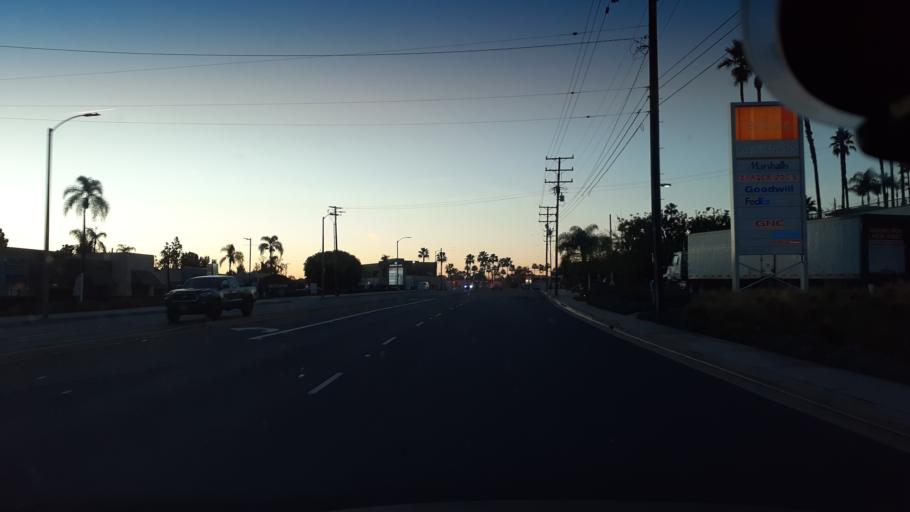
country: US
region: California
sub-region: Los Angeles County
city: San Pedro
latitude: 33.7560
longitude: -118.3099
